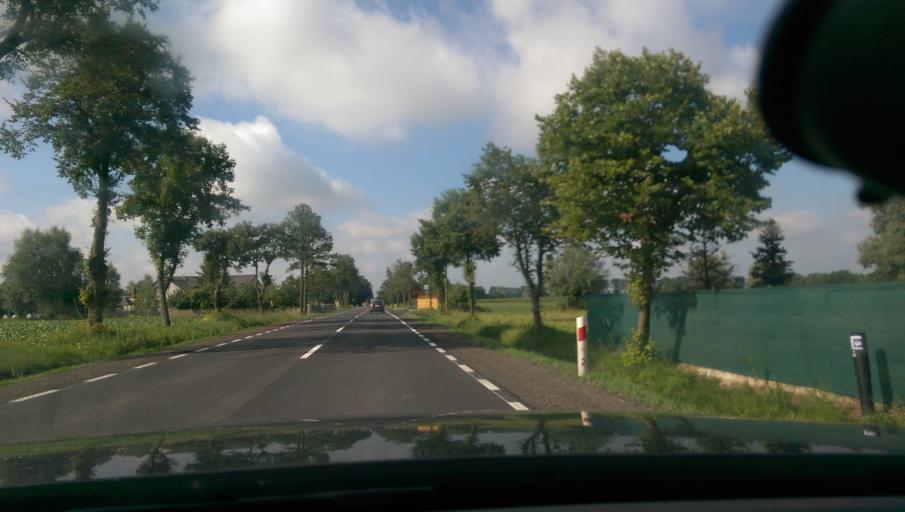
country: PL
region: Masovian Voivodeship
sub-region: Powiat ciechanowski
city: Ojrzen
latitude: 52.7342
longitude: 20.5175
